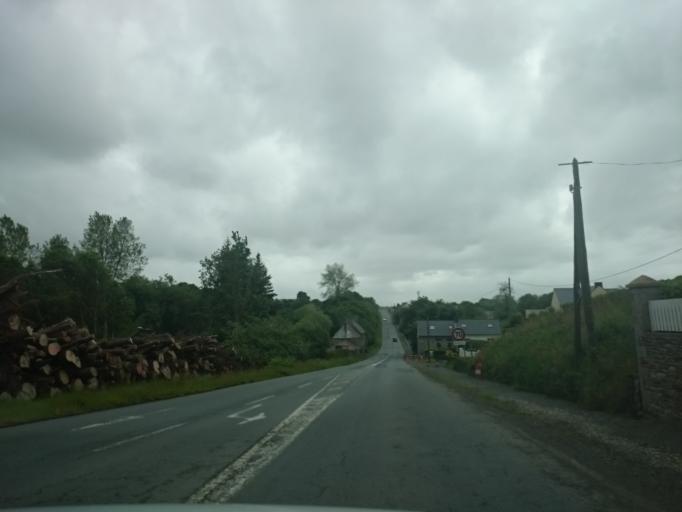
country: FR
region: Brittany
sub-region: Departement des Cotes-d'Armor
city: Lannion
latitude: 48.7395
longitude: -3.4295
